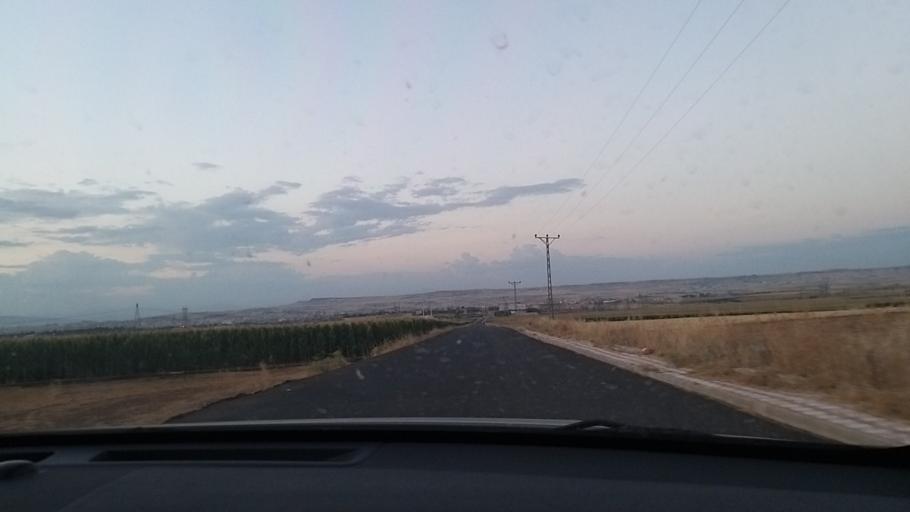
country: TR
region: Batman
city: Erkoklu
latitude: 37.8433
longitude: 41.1354
